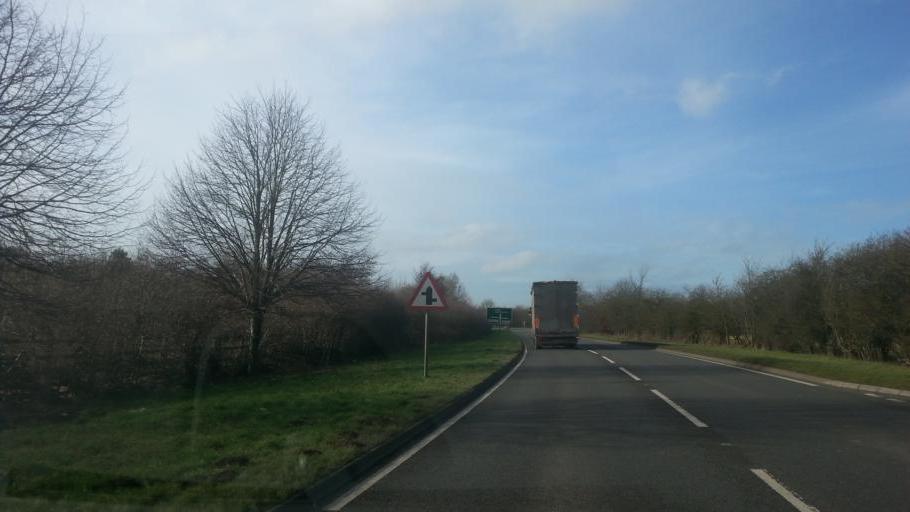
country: GB
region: England
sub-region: District of Rutland
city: Ridlington
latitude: 52.5969
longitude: -0.7878
